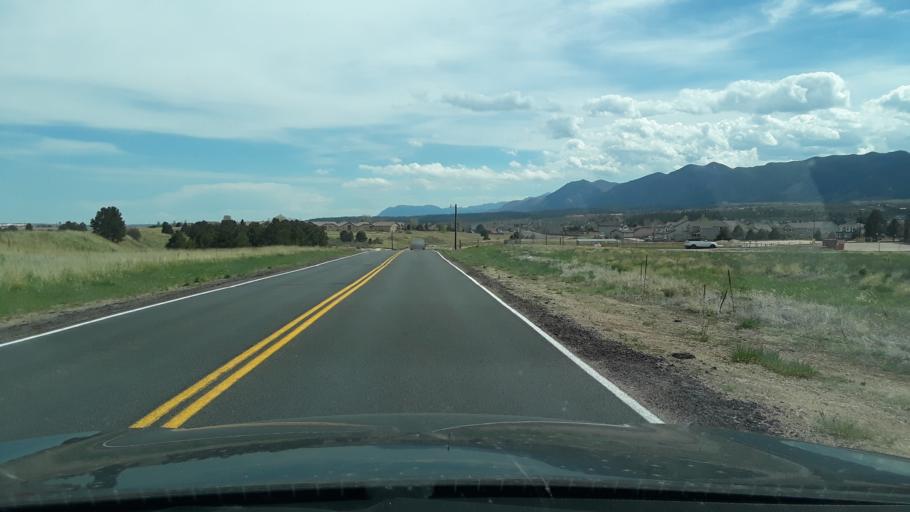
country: US
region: Colorado
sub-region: El Paso County
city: Monument
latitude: 39.0883
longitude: -104.8684
